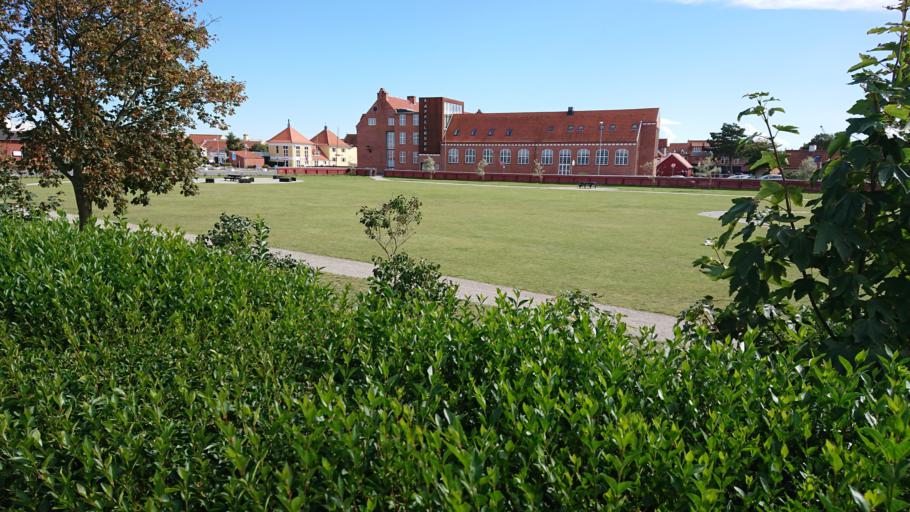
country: DK
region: North Denmark
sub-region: Frederikshavn Kommune
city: Skagen
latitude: 57.7235
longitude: 10.5857
